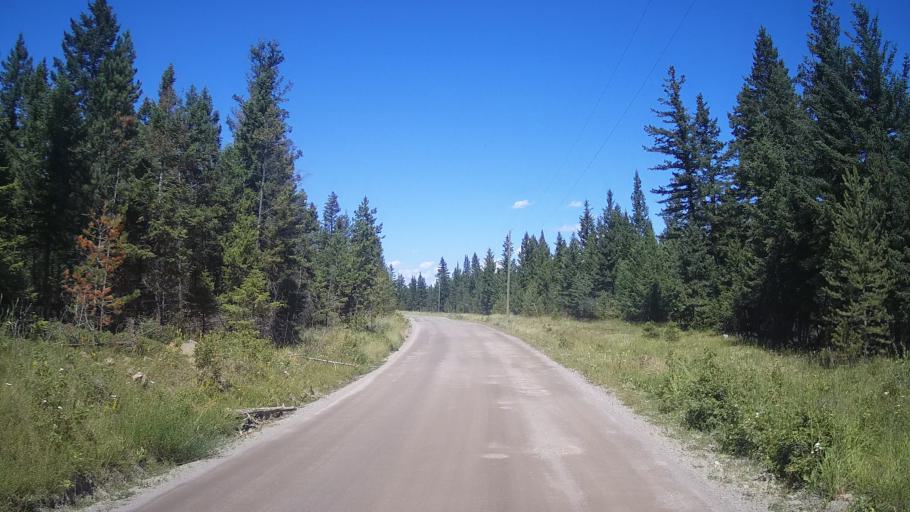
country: CA
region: British Columbia
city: Cache Creek
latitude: 51.1968
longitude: -121.5905
